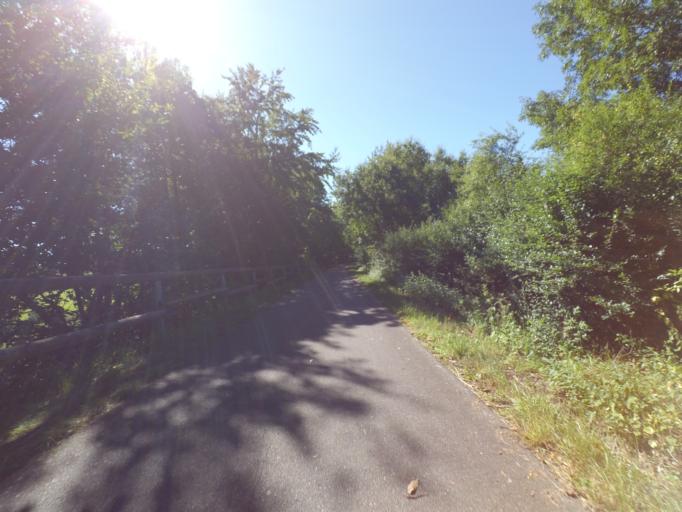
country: DE
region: Rheinland-Pfalz
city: Hasborn
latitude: 50.0499
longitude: 6.9150
